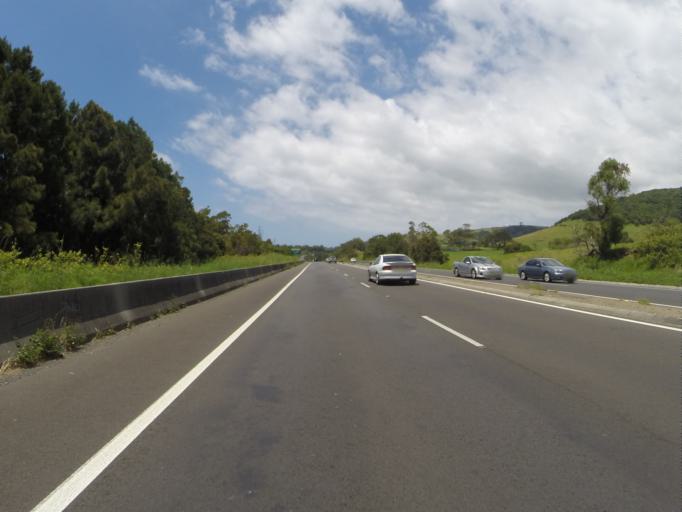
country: AU
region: New South Wales
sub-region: Kiama
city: Kiama
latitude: -34.6849
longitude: 150.8443
